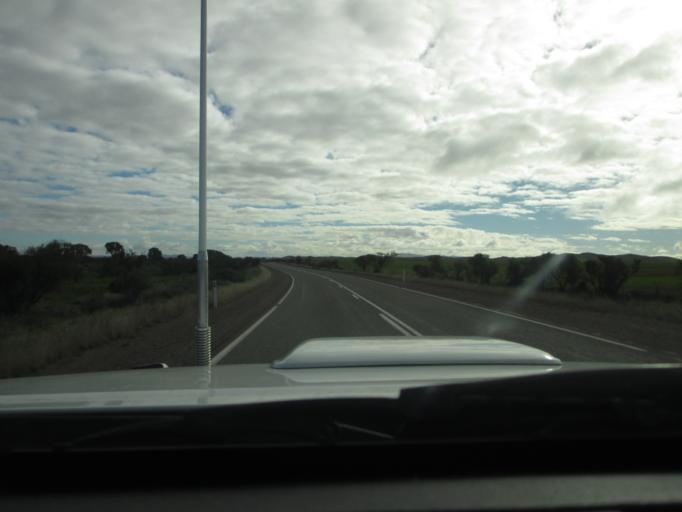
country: AU
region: South Australia
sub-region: Flinders Ranges
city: Quorn
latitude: -32.4587
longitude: 138.5378
